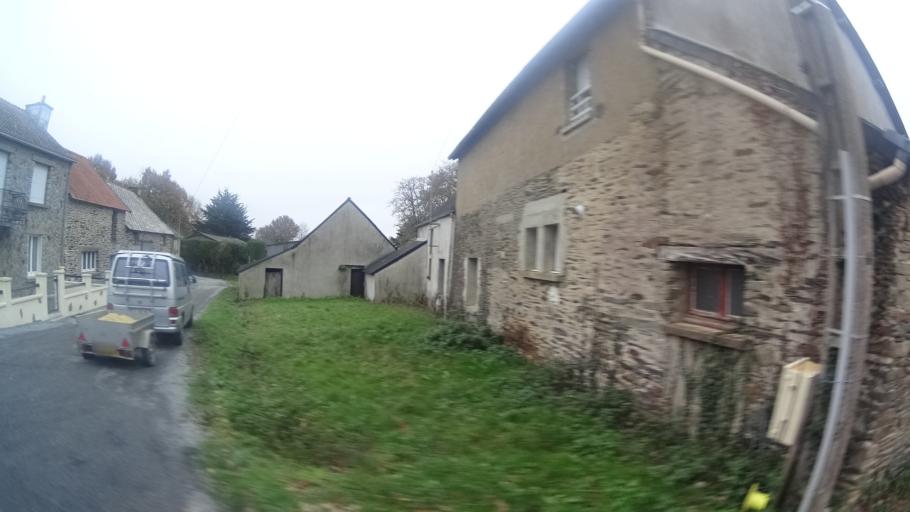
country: FR
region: Brittany
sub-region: Departement d'Ille-et-Vilaine
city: Sainte-Marie
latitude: 47.6881
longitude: -1.9982
